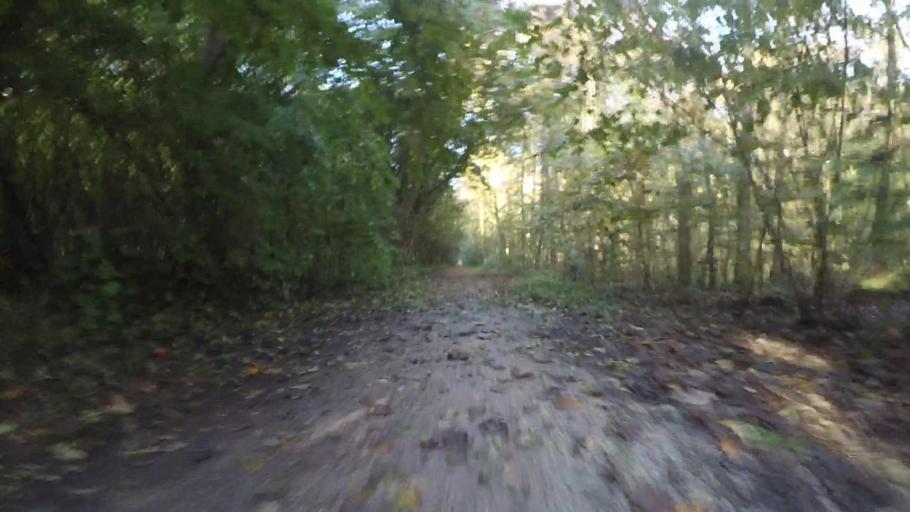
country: NL
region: Flevoland
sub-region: Gemeente Zeewolde
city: Zeewolde
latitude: 52.3010
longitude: 5.5317
